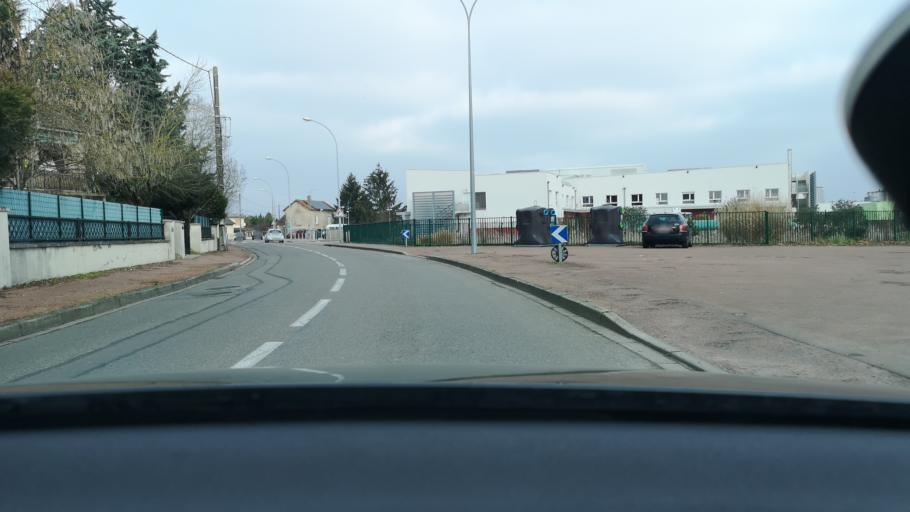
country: FR
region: Bourgogne
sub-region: Departement de Saone-et-Loire
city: Chalon-sur-Saone
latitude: 46.8013
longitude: 4.8509
